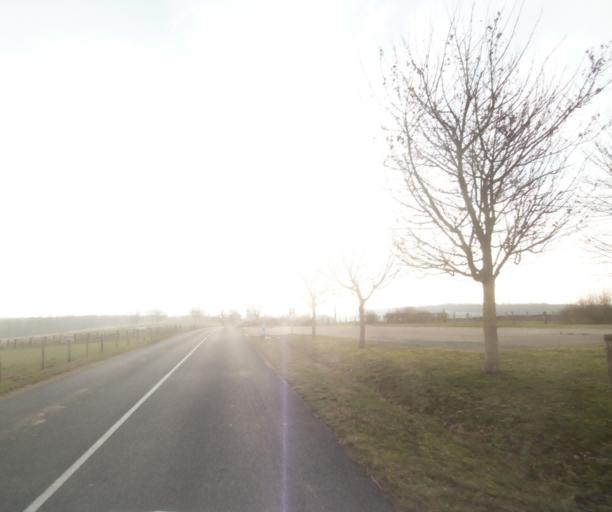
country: FR
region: Champagne-Ardenne
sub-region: Departement de la Marne
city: Sermaize-les-Bains
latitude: 48.7305
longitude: 4.9337
